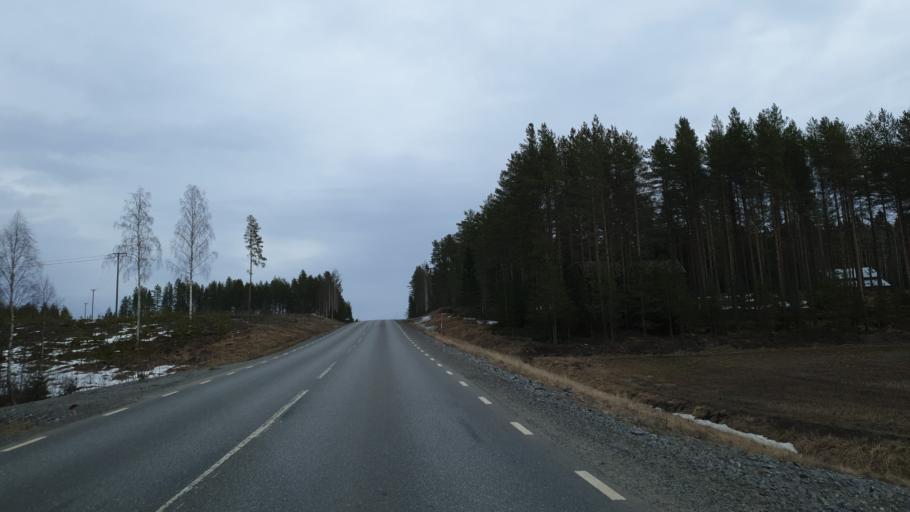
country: SE
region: Vaesterbotten
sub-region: Robertsfors Kommun
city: Robertsfors
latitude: 64.2195
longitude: 20.9063
